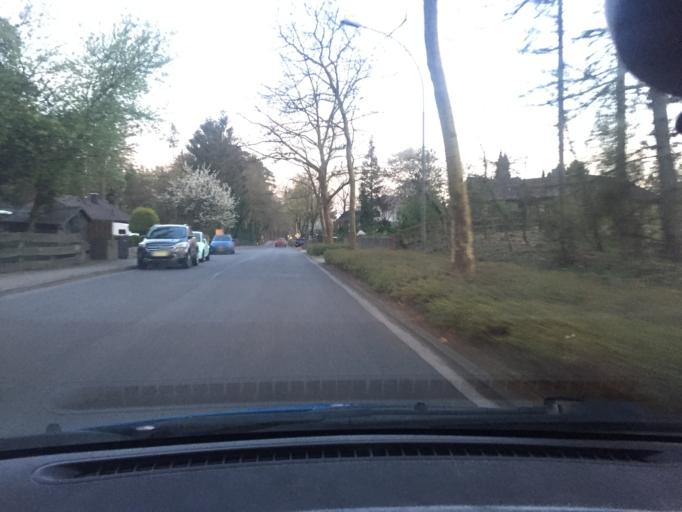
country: DE
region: Lower Saxony
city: Buchholz in der Nordheide
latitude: 53.3135
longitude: 9.8643
